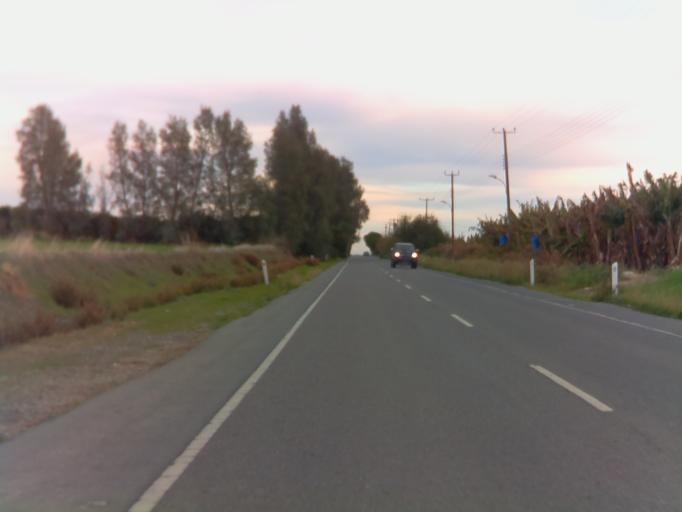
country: CY
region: Pafos
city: Pegeia
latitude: 34.8653
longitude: 32.3686
